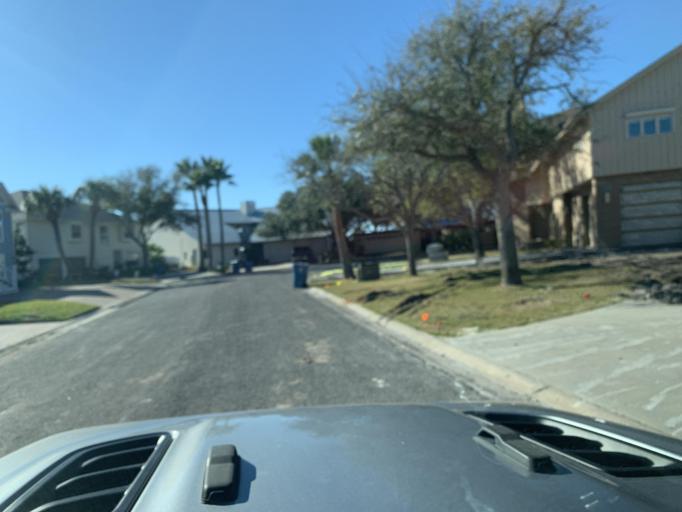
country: US
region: Texas
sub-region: Aransas County
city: Fulton
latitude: 28.0361
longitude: -97.0323
